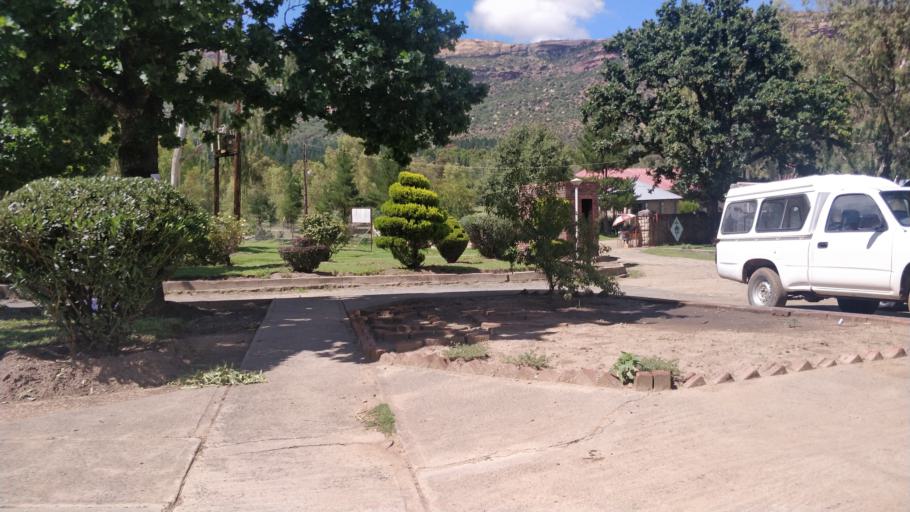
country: LS
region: Maseru
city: Nako
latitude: -29.6281
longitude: 27.5065
